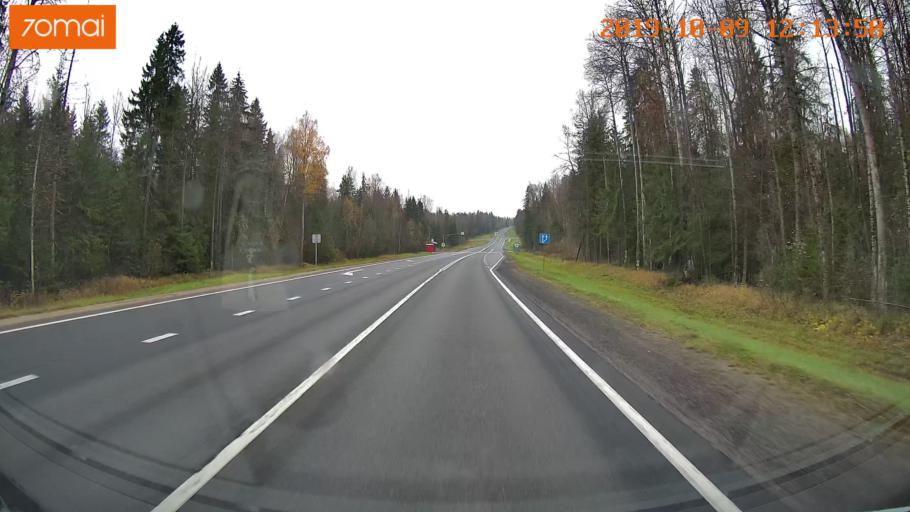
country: RU
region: Jaroslavl
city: Prechistoye
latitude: 58.5044
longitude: 40.3434
